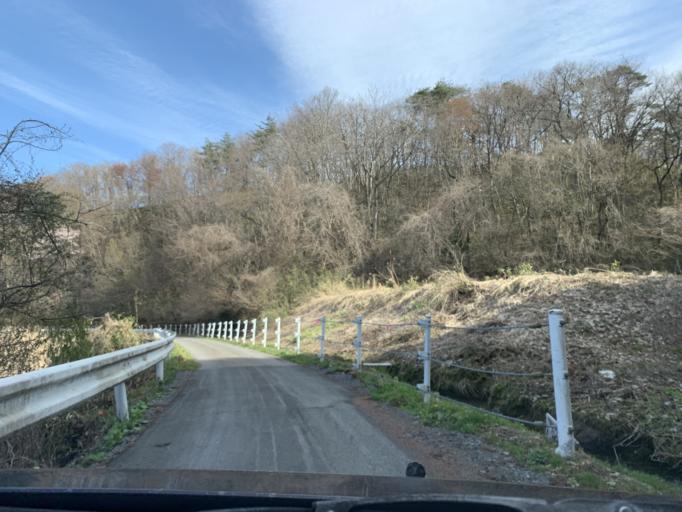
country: JP
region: Iwate
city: Ichinoseki
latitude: 38.9377
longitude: 141.0645
